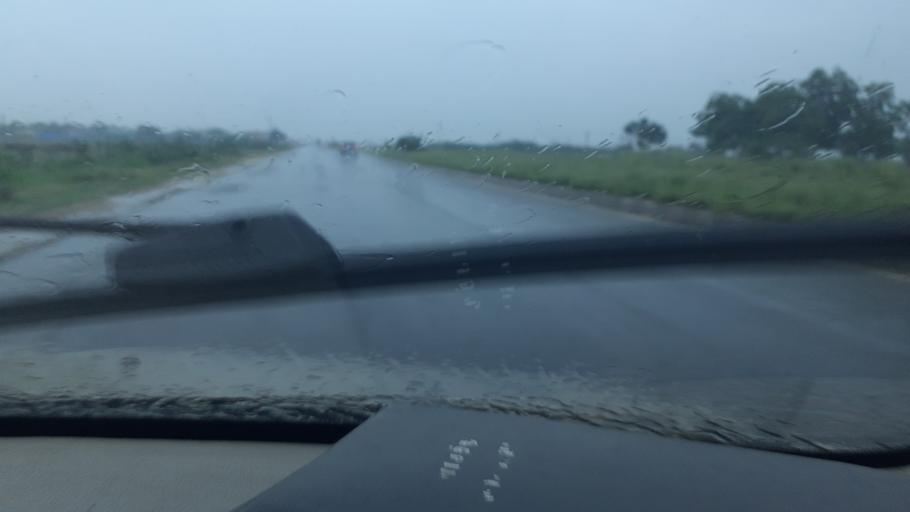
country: IN
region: Tamil Nadu
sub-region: Virudhunagar
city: Sattur
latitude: 9.4210
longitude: 77.9170
